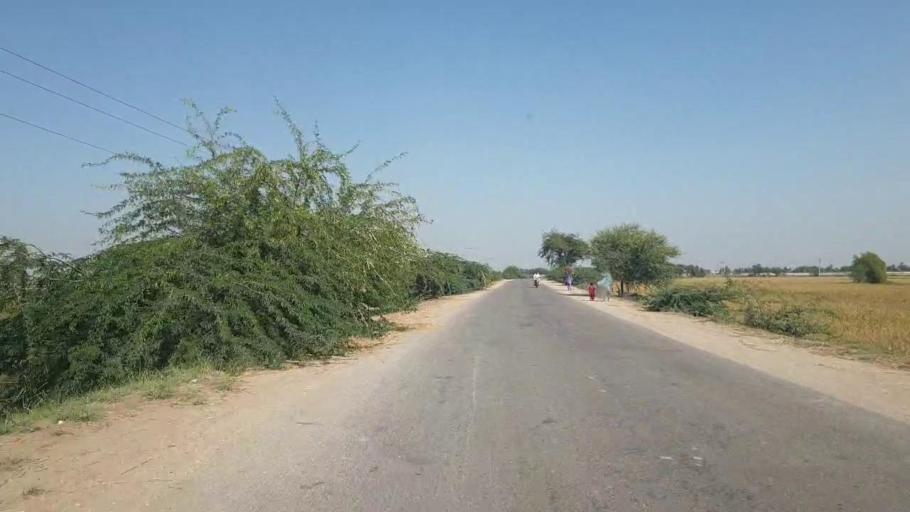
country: PK
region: Sindh
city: Talhar
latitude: 24.9012
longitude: 68.8293
